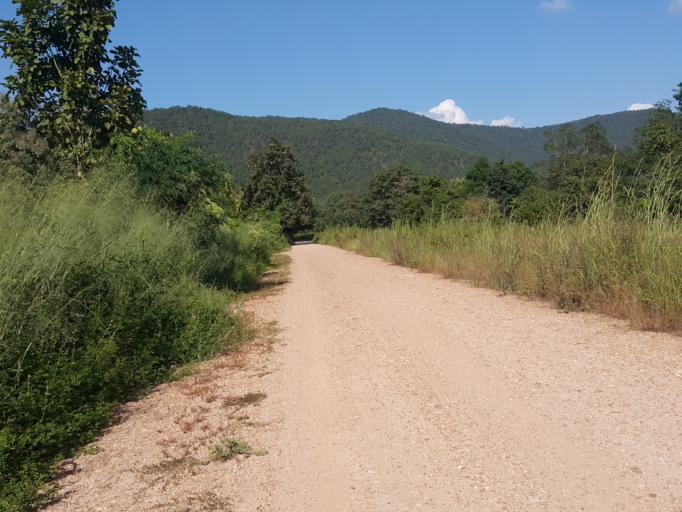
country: TH
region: Chiang Mai
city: Mae On
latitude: 18.7840
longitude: 99.1999
